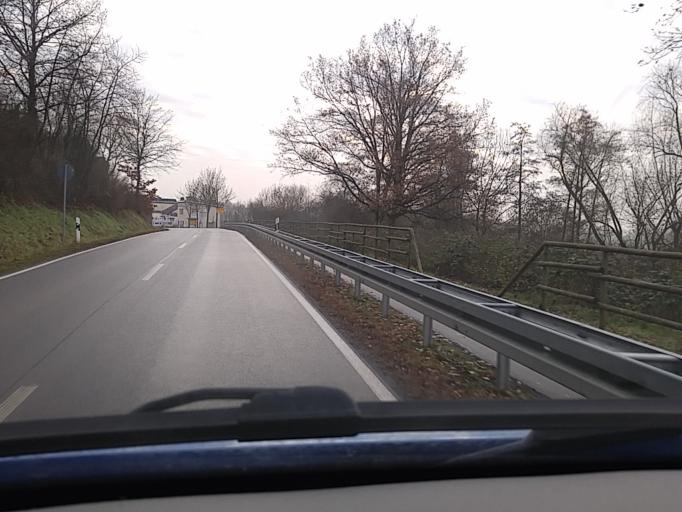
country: DE
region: Hesse
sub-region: Regierungsbezirk Darmstadt
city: Bad Nauheim
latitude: 50.3787
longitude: 8.7600
